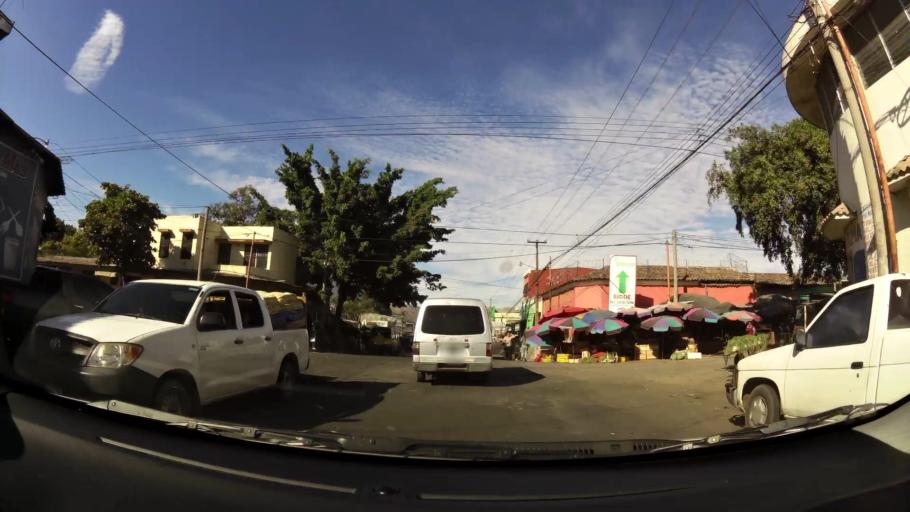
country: SV
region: Santa Ana
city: Santa Ana
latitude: 13.9873
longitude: -89.5656
